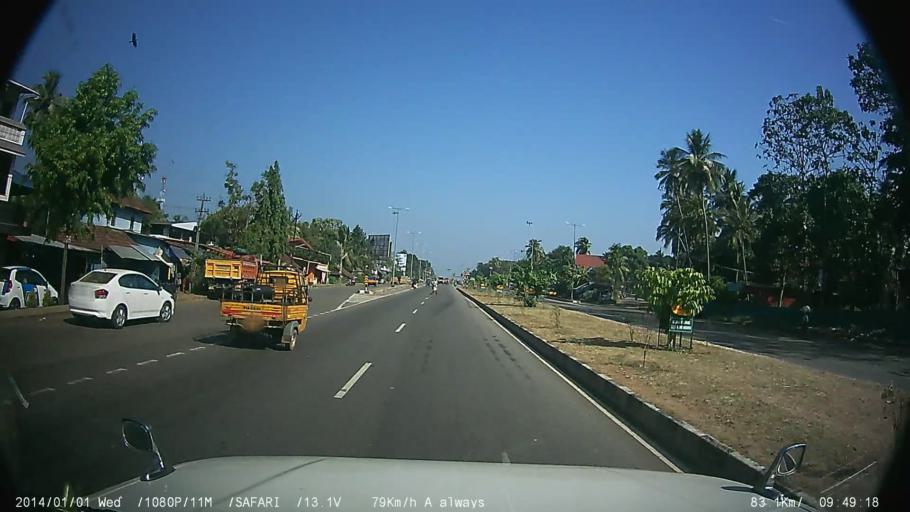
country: IN
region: Kerala
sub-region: Thrissur District
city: Trichur
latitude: 10.5086
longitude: 76.2583
